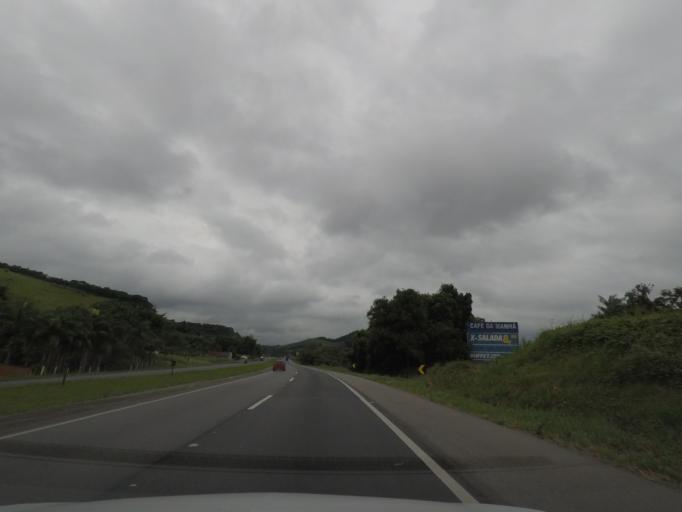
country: BR
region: Sao Paulo
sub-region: Juquia
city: Juquia
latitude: -24.3576
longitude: -47.6859
